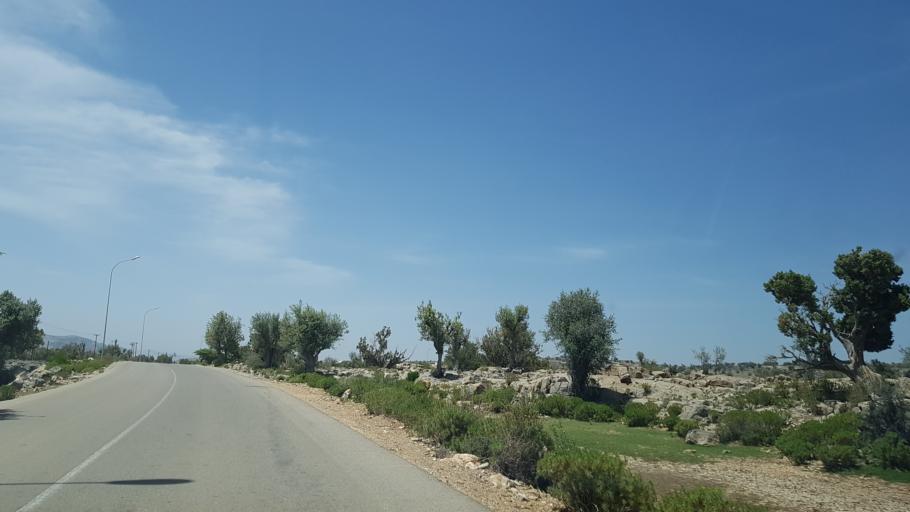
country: OM
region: Al Batinah
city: Bayt al `Awabi
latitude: 23.1299
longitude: 57.5974
